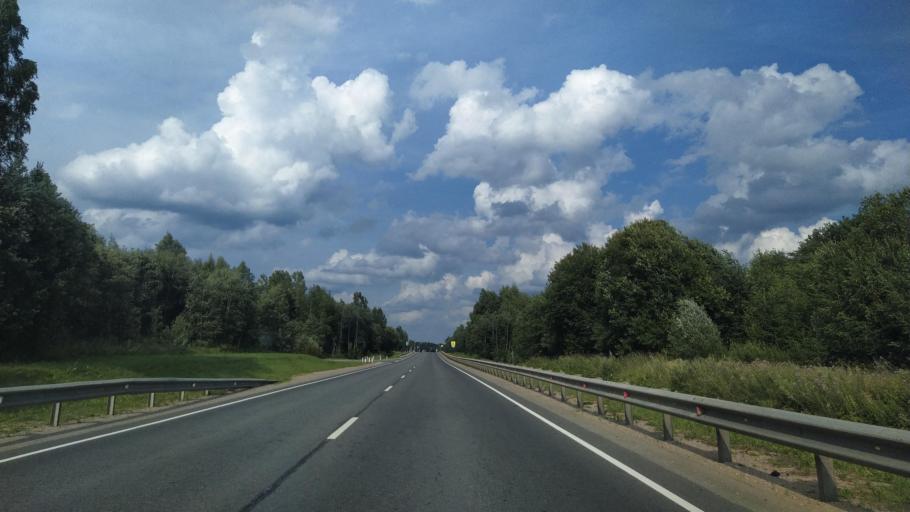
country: RU
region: Novgorod
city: Sol'tsy
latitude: 58.1541
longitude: 30.4396
